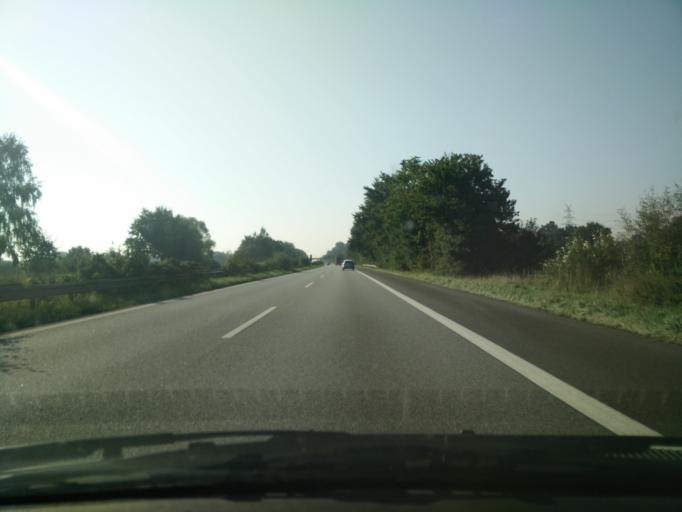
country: DE
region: Schleswig-Holstein
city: Kummerfeld
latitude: 53.6938
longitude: 9.7809
